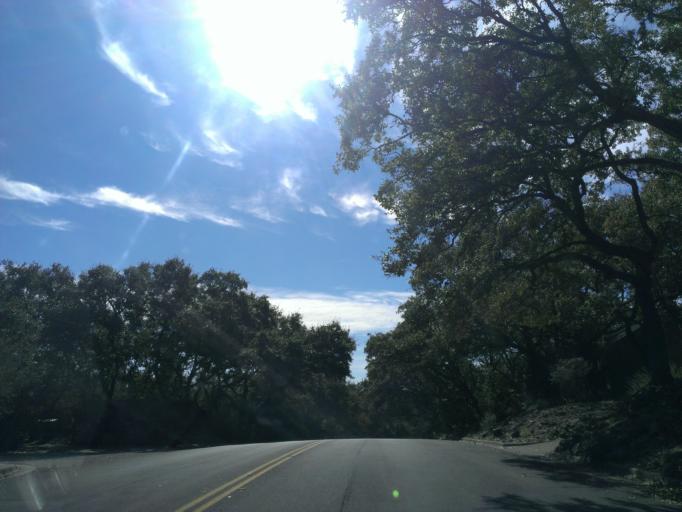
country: US
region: Texas
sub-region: Travis County
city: West Lake Hills
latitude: 30.3092
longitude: -97.7680
